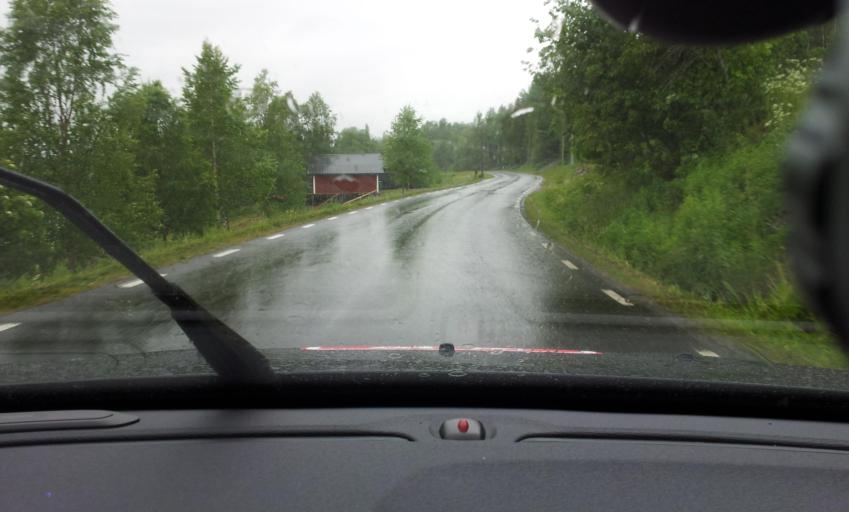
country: SE
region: Jaemtland
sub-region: Are Kommun
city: Are
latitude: 63.3132
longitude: 13.1750
